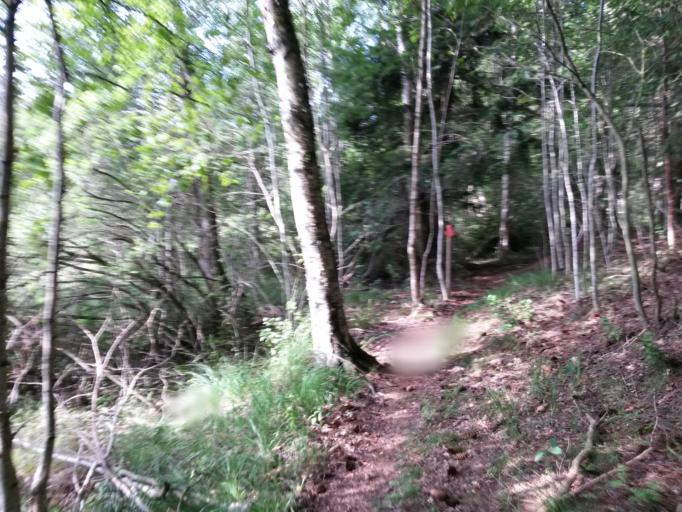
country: SE
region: Vaestra Goetaland
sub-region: Vargarda Kommun
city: Vargarda
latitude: 58.0480
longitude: 12.8235
